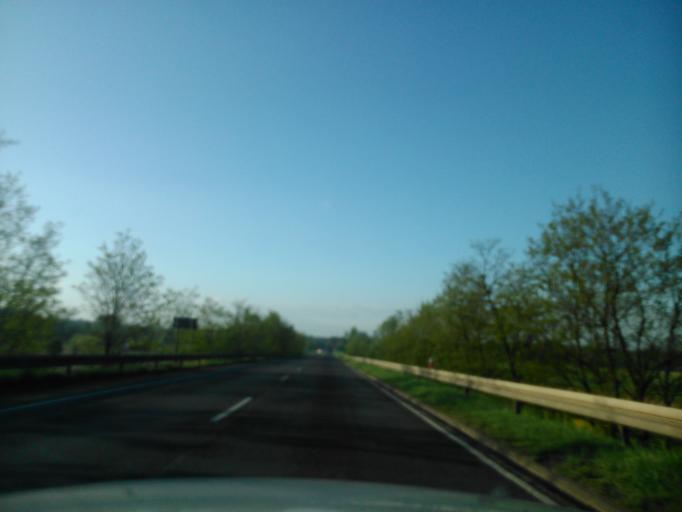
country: PL
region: Masovian Voivodeship
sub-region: Powiat plocki
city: Wyszogrod
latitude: 52.3721
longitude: 20.1900
